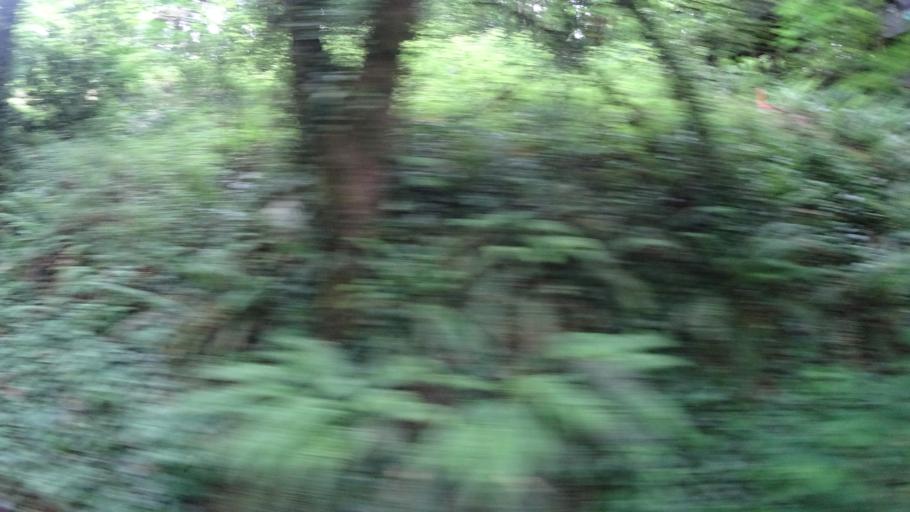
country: US
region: Oregon
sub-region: Multnomah County
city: Portland
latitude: 45.4886
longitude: -122.6980
